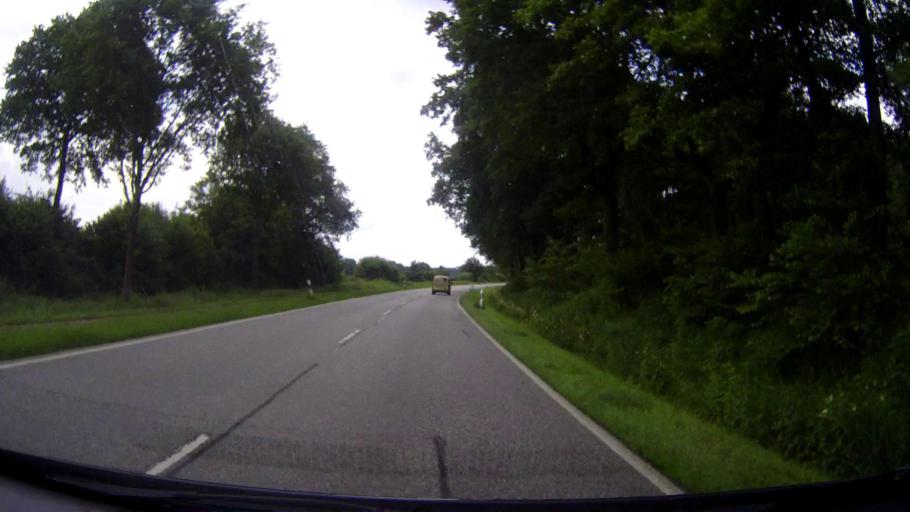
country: DE
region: Schleswig-Holstein
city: Tappendorf
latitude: 54.0845
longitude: 9.6867
